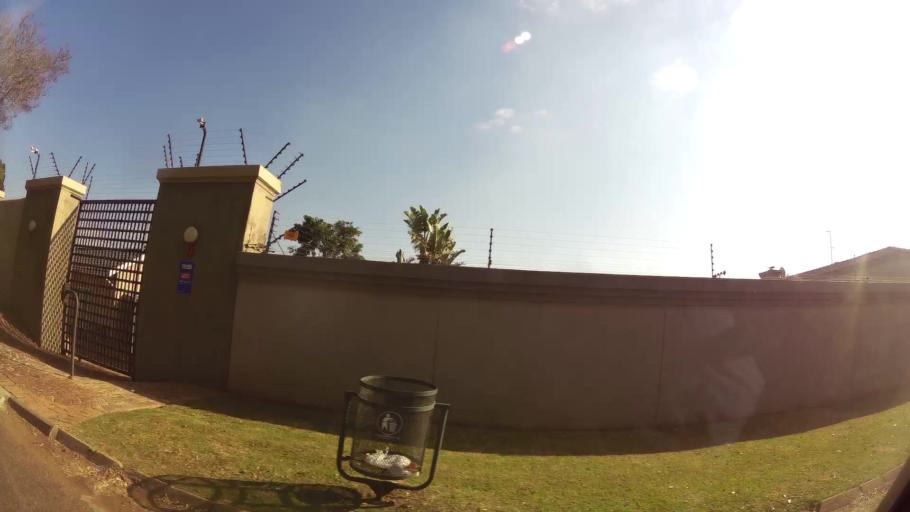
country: ZA
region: Gauteng
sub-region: Ekurhuleni Metropolitan Municipality
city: Germiston
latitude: -26.1810
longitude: 28.1436
